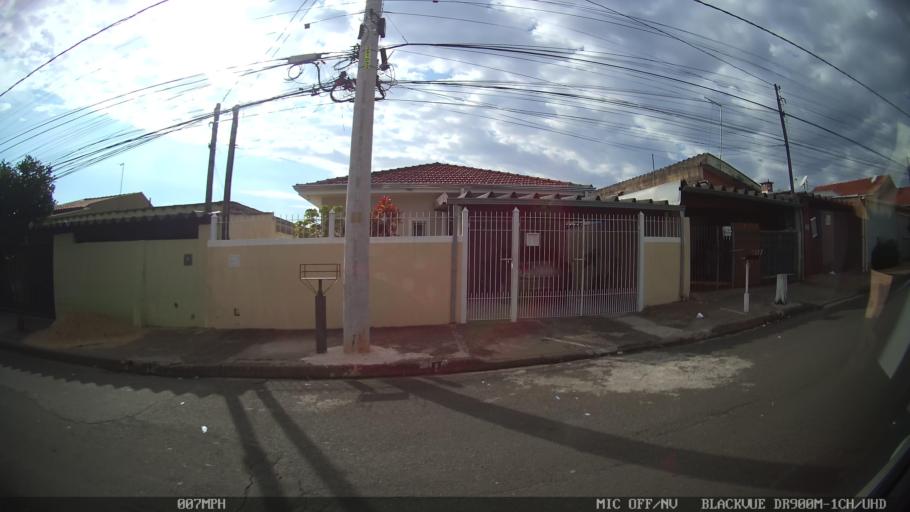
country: BR
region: Sao Paulo
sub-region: Americana
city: Americana
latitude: -22.7196
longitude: -47.3660
